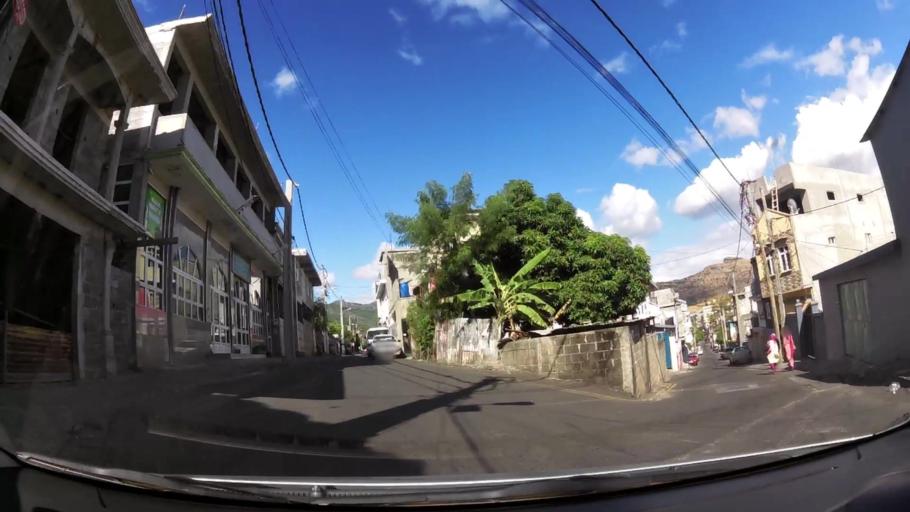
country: MU
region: Port Louis
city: Port Louis
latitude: -20.1587
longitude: 57.5194
